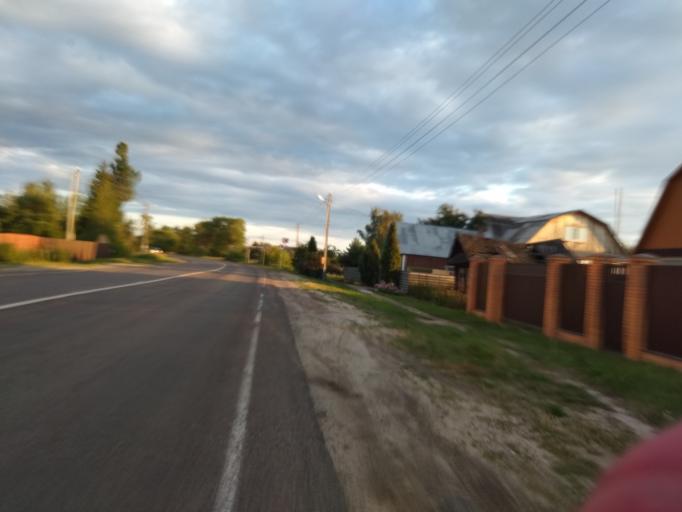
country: RU
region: Moskovskaya
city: Kerva
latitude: 55.5932
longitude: 39.7012
